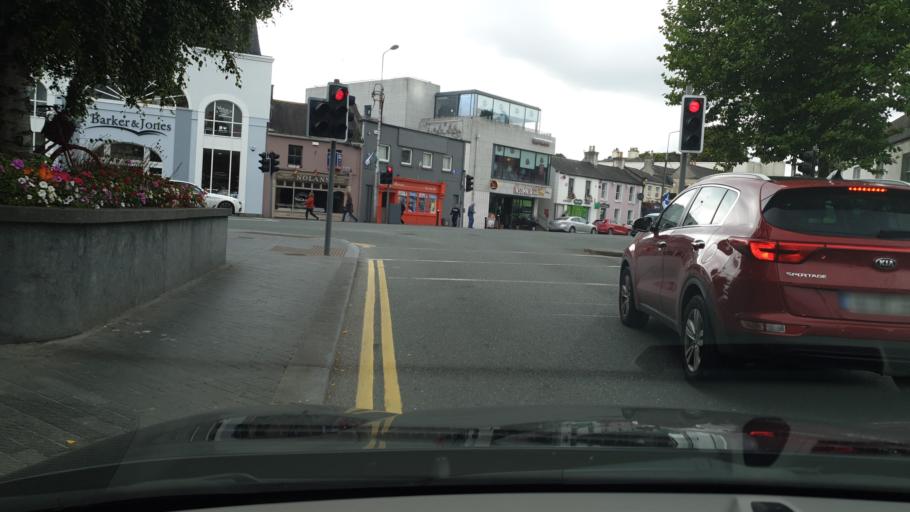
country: IE
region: Leinster
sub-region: Kildare
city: Naas
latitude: 53.2197
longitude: -6.6618
